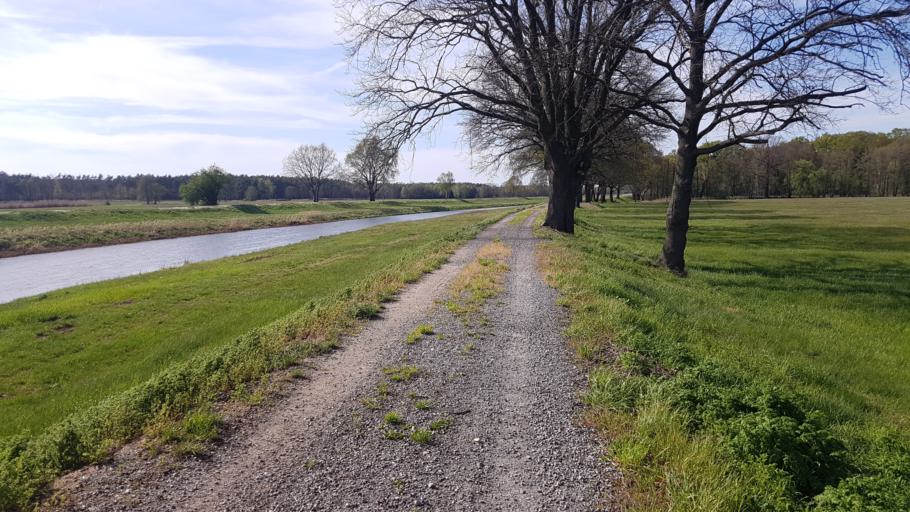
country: DE
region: Brandenburg
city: Falkenberg
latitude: 51.6197
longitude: 13.2901
